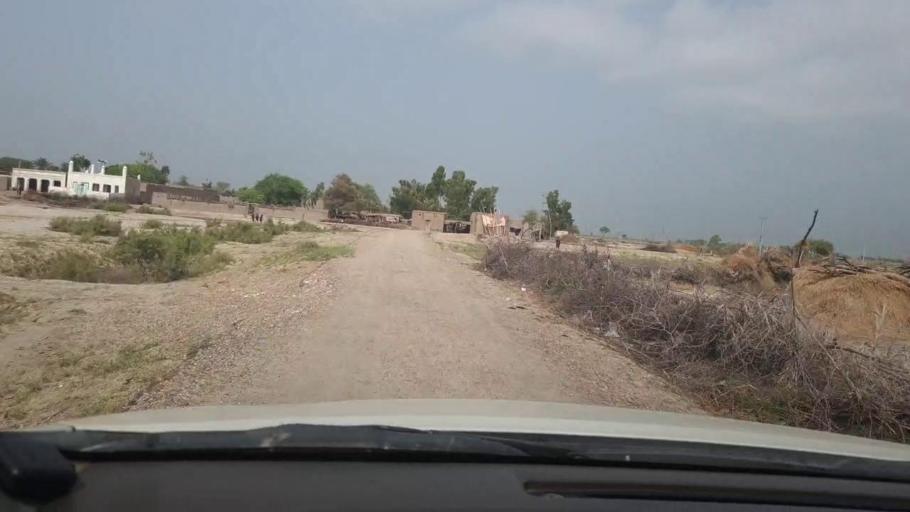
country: PK
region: Sindh
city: Shikarpur
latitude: 28.0252
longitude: 68.5849
